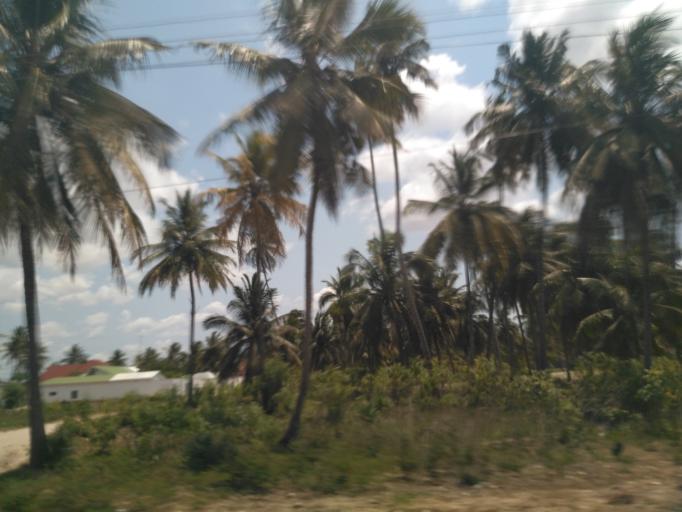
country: TZ
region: Dar es Salaam
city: Dar es Salaam
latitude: -6.8306
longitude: 39.3367
